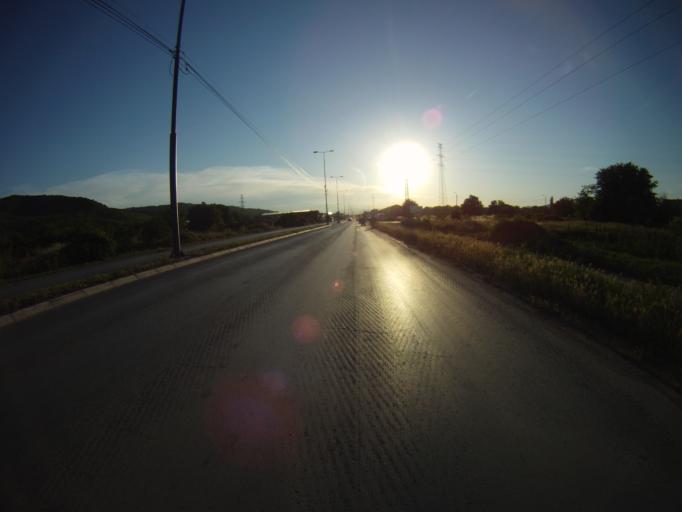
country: RS
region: Central Serbia
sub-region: Nisavski Okrug
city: Niska Banja
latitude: 43.3045
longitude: 21.9714
